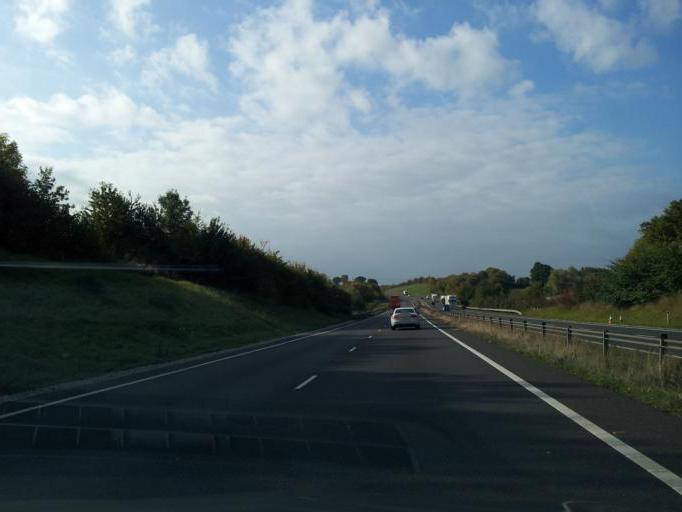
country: GB
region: England
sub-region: Northamptonshire
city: Silverstone
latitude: 52.1047
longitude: -1.0086
